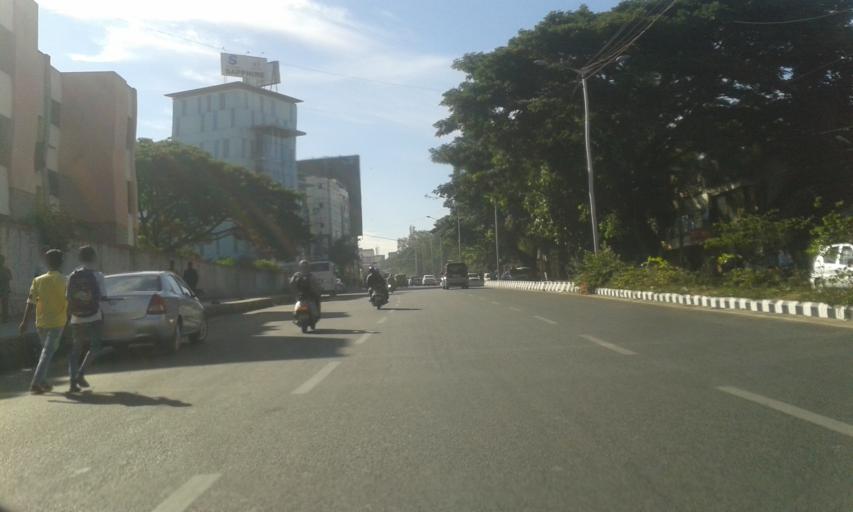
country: IN
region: Karnataka
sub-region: Bangalore Urban
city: Bangalore
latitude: 12.9459
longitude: 77.6071
